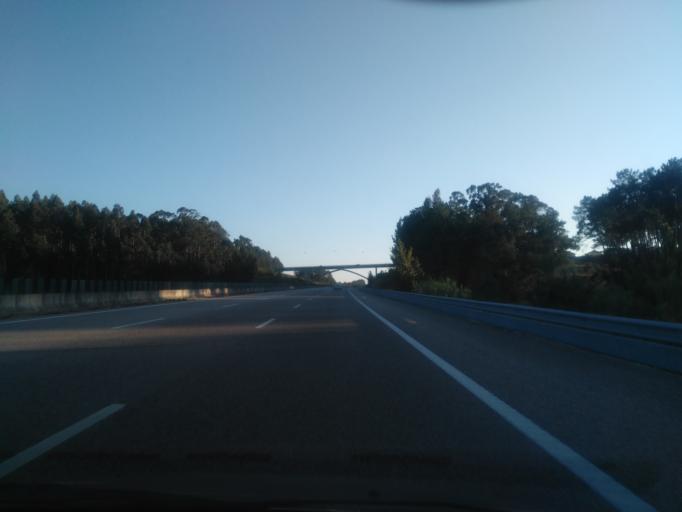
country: PT
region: Coimbra
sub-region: Figueira da Foz
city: Lavos
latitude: 40.0833
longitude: -8.7684
